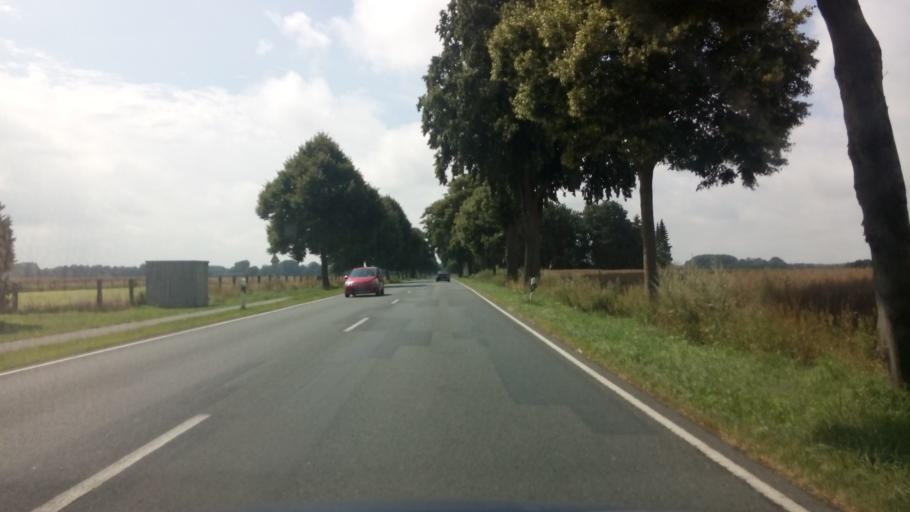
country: DE
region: Lower Saxony
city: Twistringen
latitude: 52.7820
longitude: 8.6194
